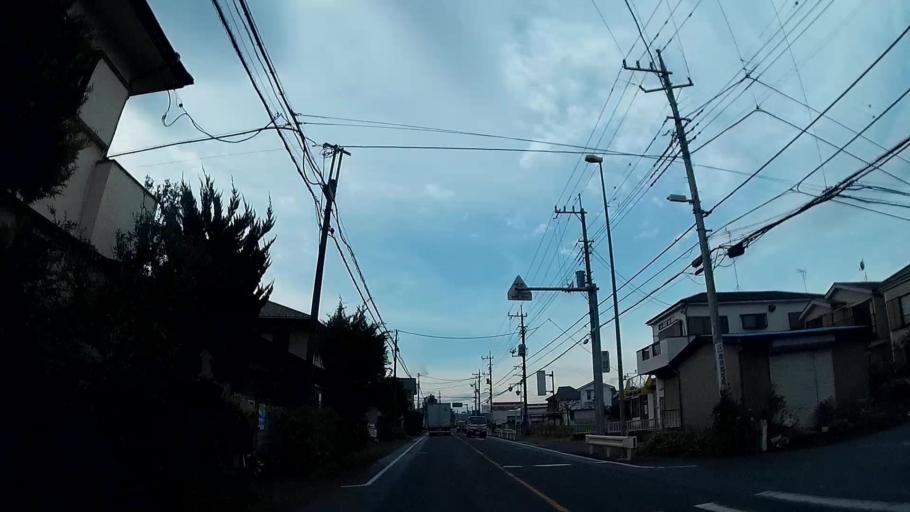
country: JP
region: Saitama
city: Sayama
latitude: 35.8487
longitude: 139.3709
